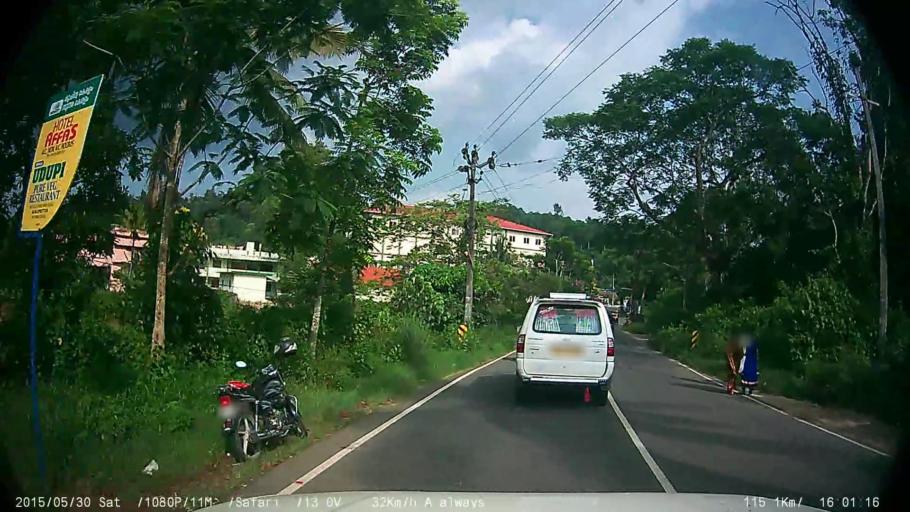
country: IN
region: Kerala
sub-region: Wayanad
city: Kalpetta
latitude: 11.6347
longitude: 76.0884
